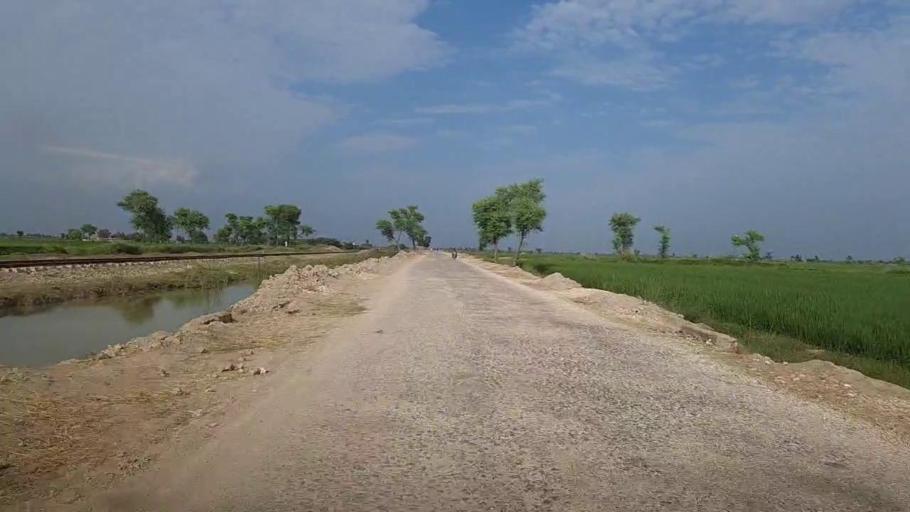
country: PK
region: Sindh
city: Thul
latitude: 28.2683
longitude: 68.8303
